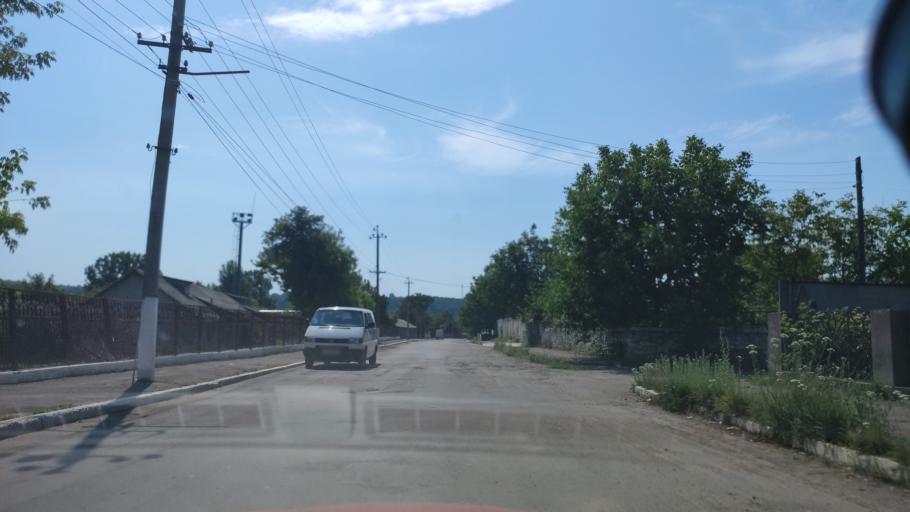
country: MD
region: Raionul Soroca
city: Soroca
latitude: 48.1729
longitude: 28.3144
